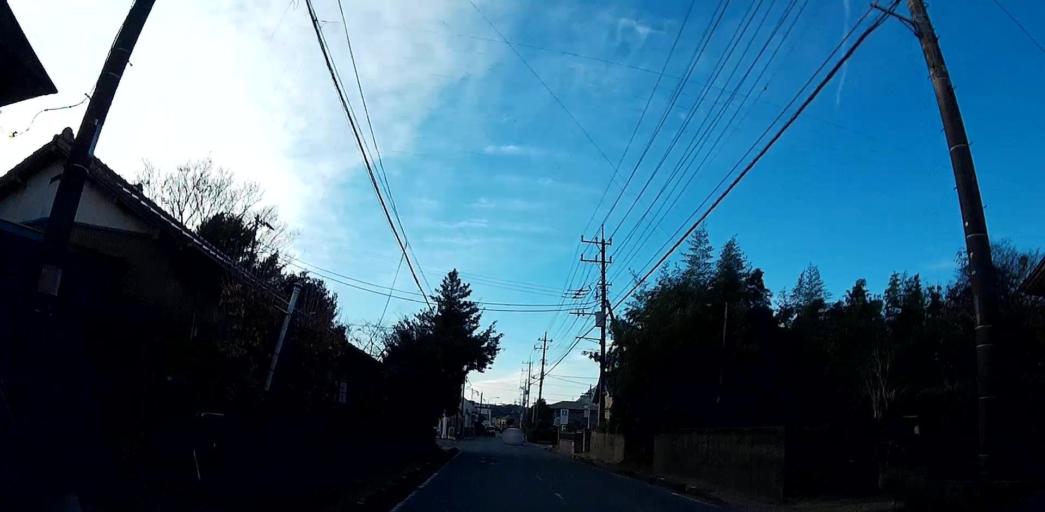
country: JP
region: Chiba
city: Omigawa
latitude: 35.8398
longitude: 140.6653
